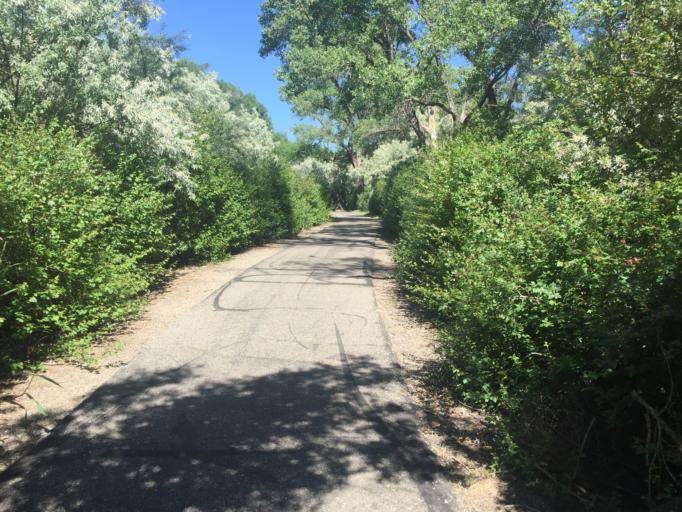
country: US
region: Colorado
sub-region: Mesa County
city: Redlands
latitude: 39.0714
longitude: -108.6011
